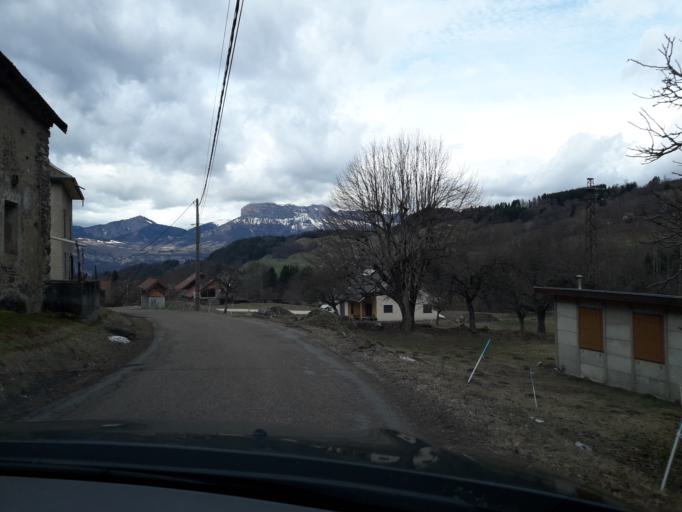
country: FR
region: Rhone-Alpes
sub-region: Departement de l'Isere
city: Le Champ-pres-Froges
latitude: 45.2457
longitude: 5.9627
